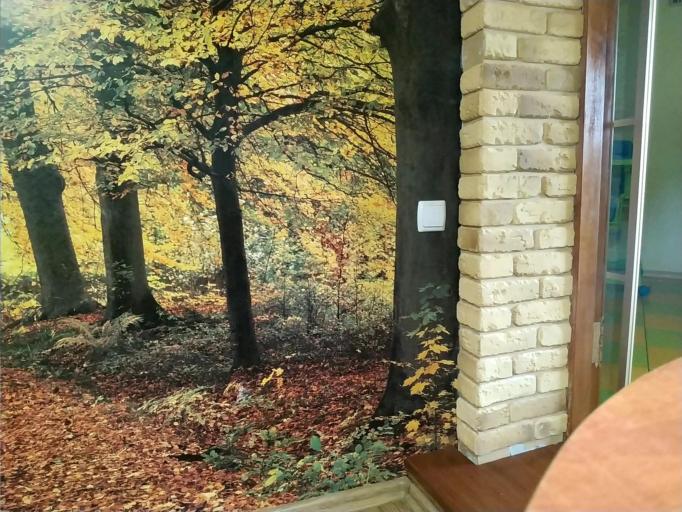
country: RU
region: Smolensk
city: Dorogobuzh
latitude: 54.9497
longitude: 33.2930
